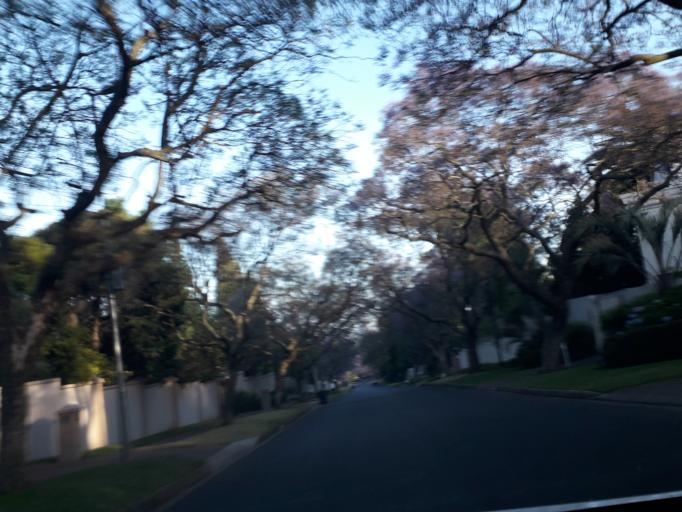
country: ZA
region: Gauteng
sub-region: City of Johannesburg Metropolitan Municipality
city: Johannesburg
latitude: -26.1359
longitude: 28.0798
